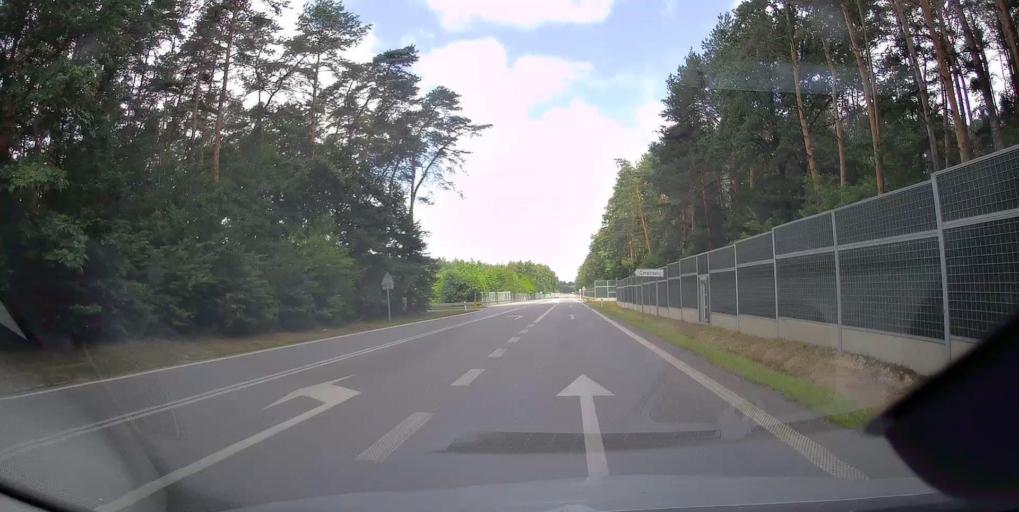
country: PL
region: Subcarpathian Voivodeship
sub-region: Powiat mielecki
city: Mielec
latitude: 50.2869
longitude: 21.4968
